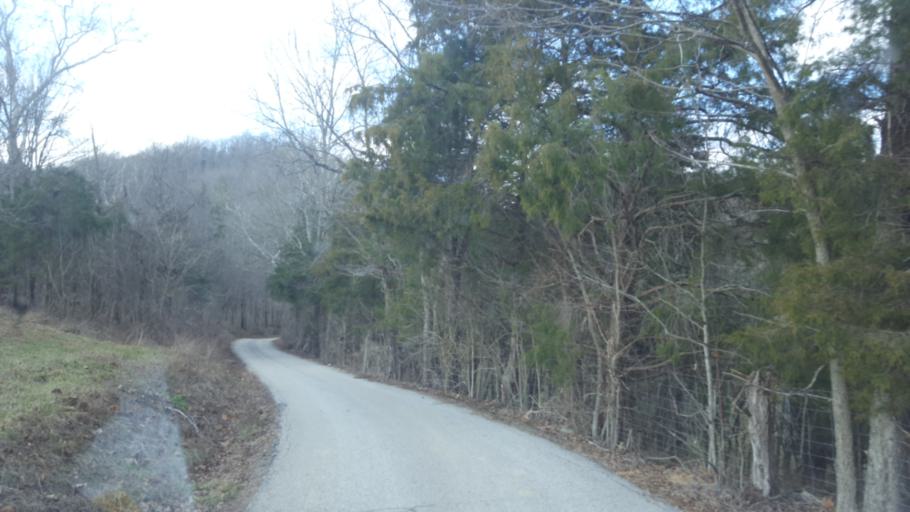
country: US
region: Kentucky
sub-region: Franklin County
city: Frankfort
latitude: 38.3695
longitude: -84.8885
